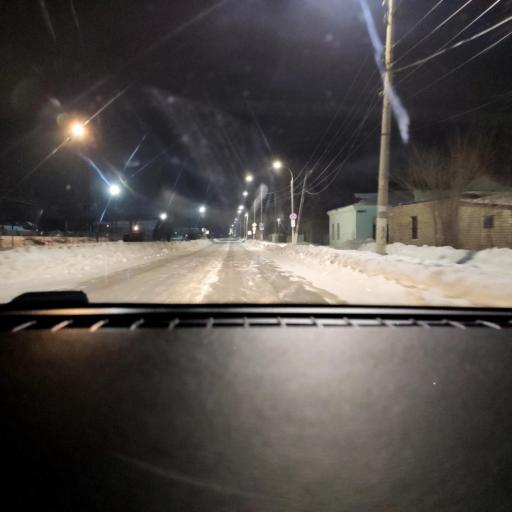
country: RU
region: Samara
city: Chapayevsk
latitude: 52.9796
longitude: 49.7037
